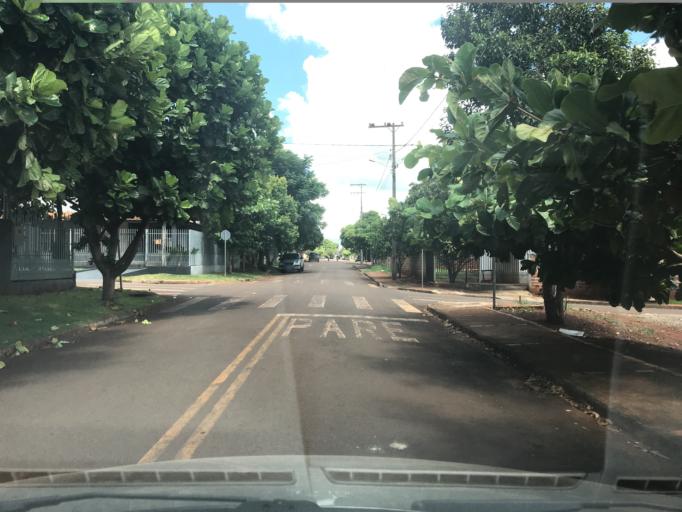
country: BR
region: Parana
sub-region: Palotina
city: Palotina
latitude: -24.2677
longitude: -53.8463
